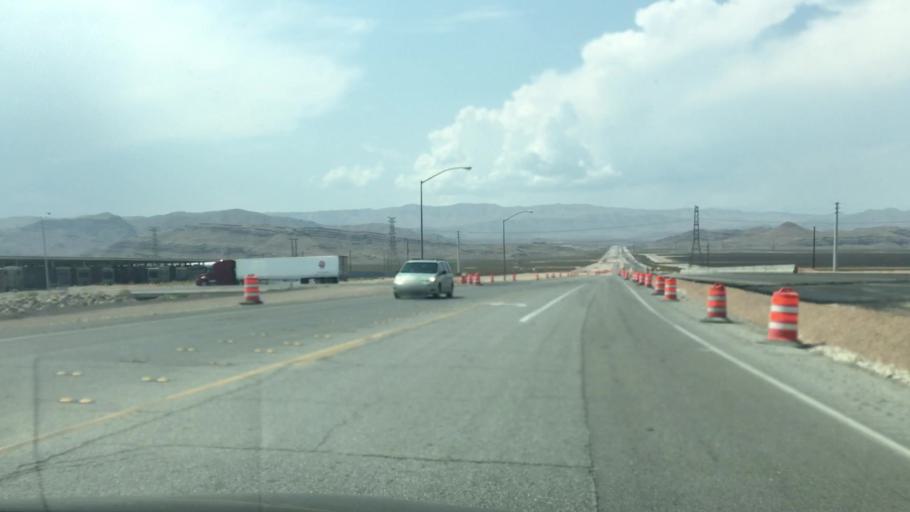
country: US
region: Nevada
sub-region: Clark County
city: Nellis Air Force Base
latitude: 36.3826
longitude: -114.8951
